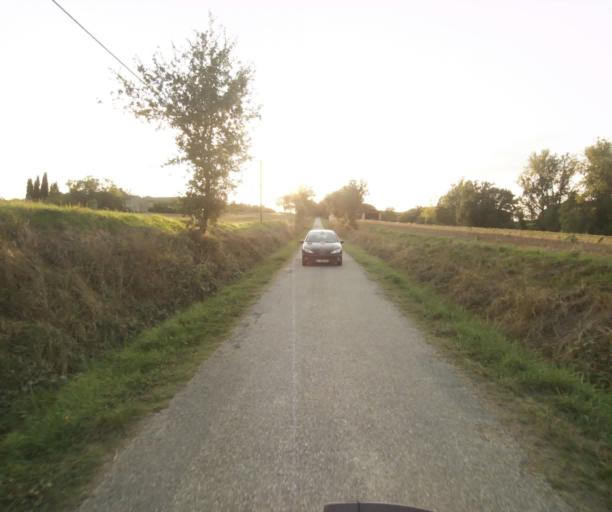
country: FR
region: Midi-Pyrenees
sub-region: Departement du Tarn-et-Garonne
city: Verdun-sur-Garonne
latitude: 43.8288
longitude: 1.1907
